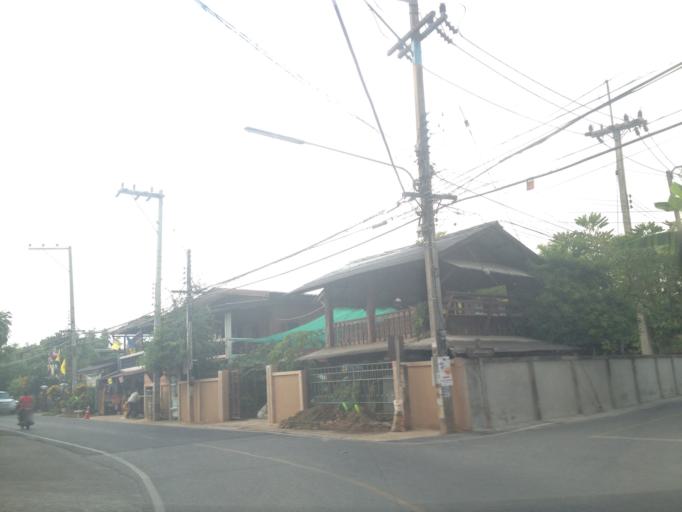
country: TH
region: Chiang Mai
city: Chiang Mai
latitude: 18.7433
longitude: 98.9467
